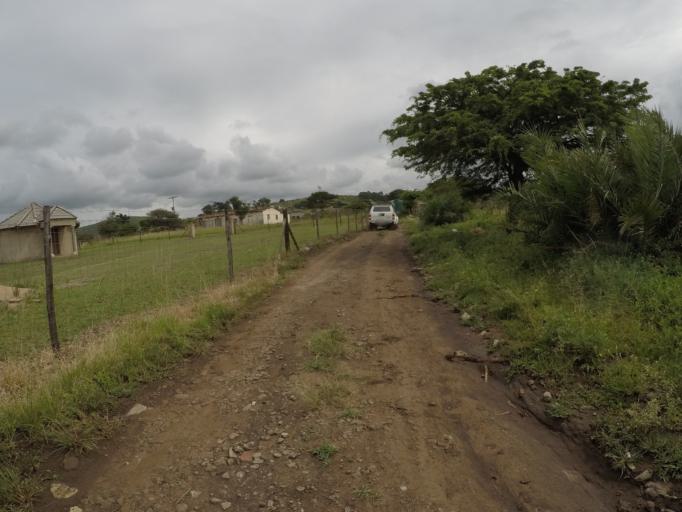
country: ZA
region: KwaZulu-Natal
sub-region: uThungulu District Municipality
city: Empangeni
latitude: -28.7128
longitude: 31.8537
